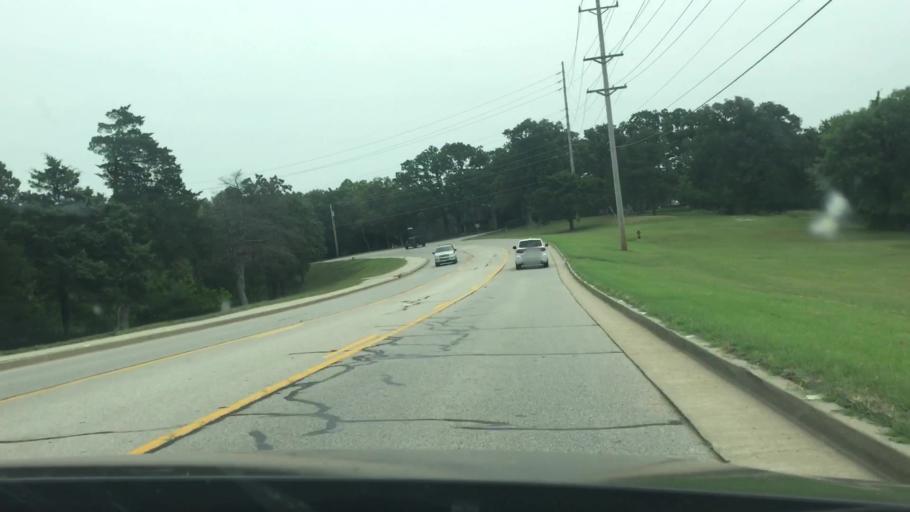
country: US
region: Missouri
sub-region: Camden County
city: Four Seasons
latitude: 38.1907
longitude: -92.6818
